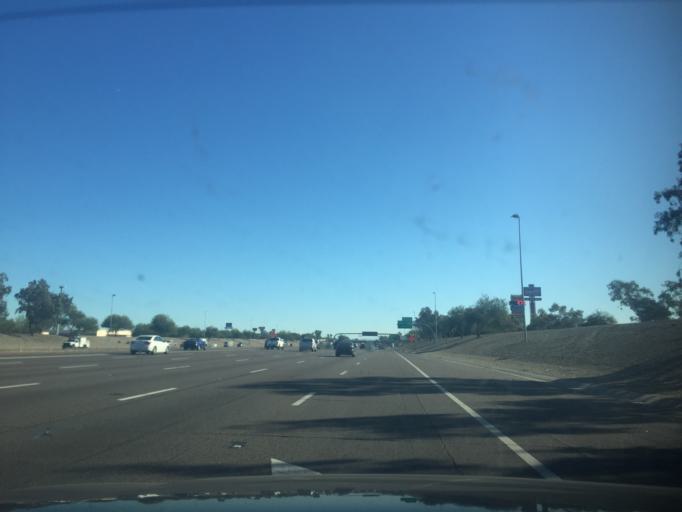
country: US
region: Arizona
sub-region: Maricopa County
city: Tolleson
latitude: 33.4620
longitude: -112.2494
